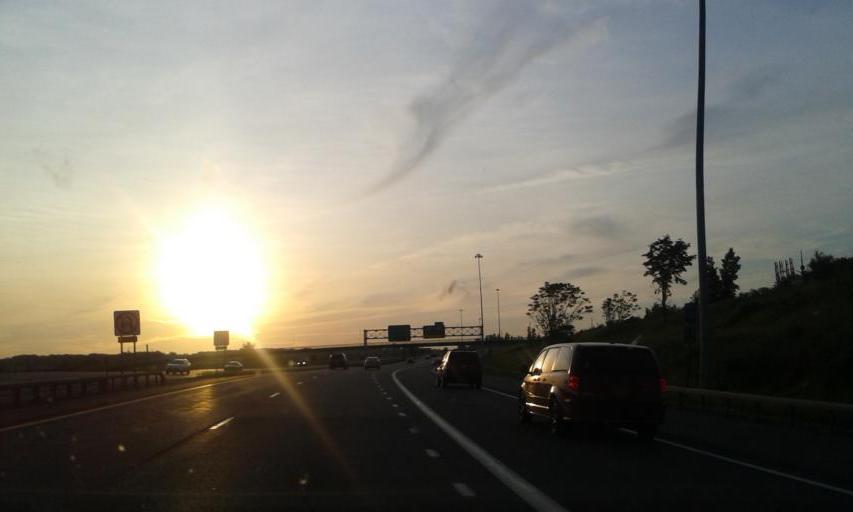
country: US
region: New York
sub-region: Onondaga County
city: Solvay
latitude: 43.0725
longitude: -76.2081
